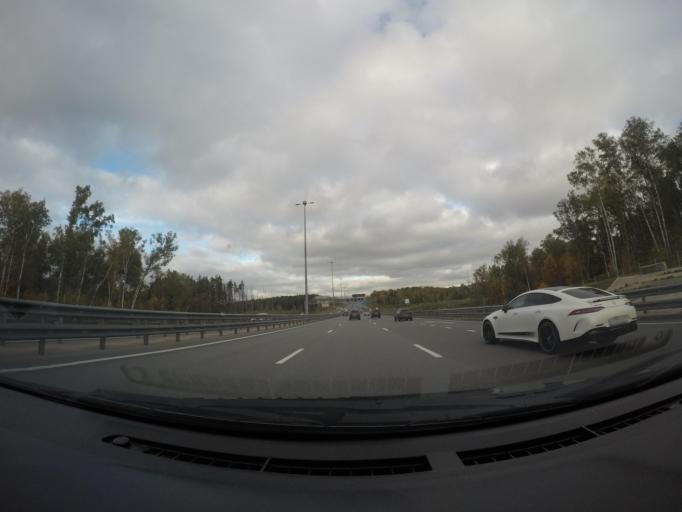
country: RU
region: Moskovskaya
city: Odintsovo
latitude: 55.6819
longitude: 37.2367
